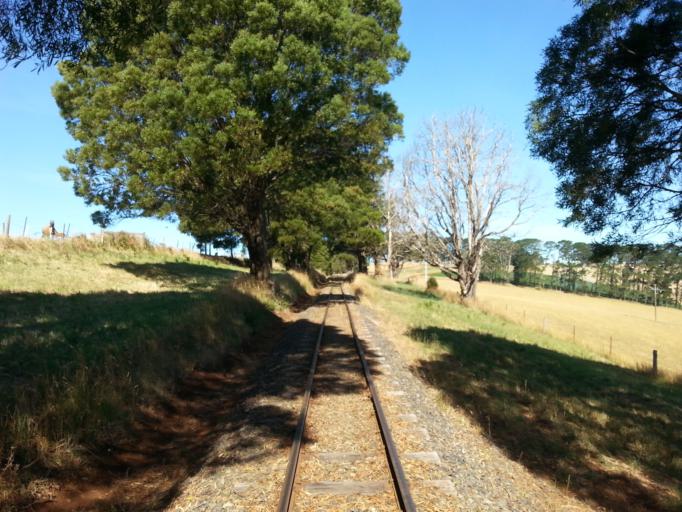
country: AU
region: Victoria
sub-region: Cardinia
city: Cockatoo
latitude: -37.9467
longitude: 145.5186
